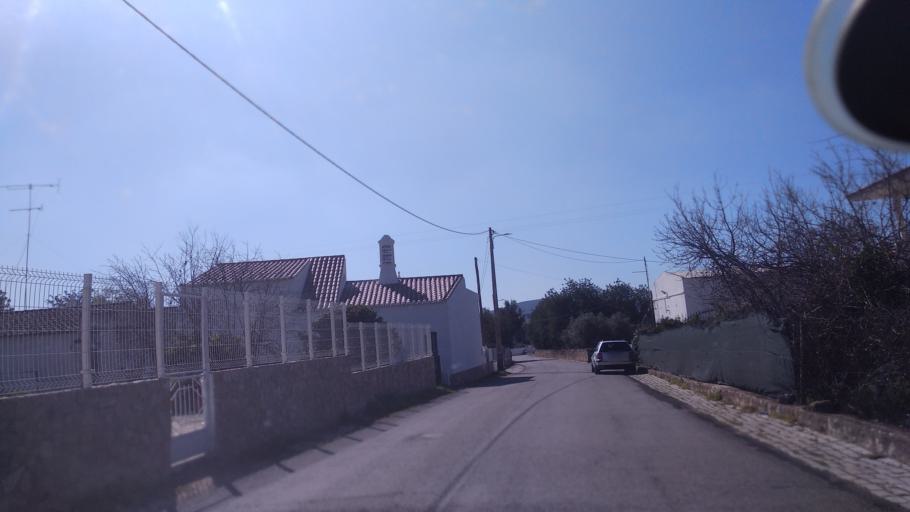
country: PT
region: Faro
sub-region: Sao Bras de Alportel
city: Sao Bras de Alportel
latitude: 37.1232
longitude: -7.9229
